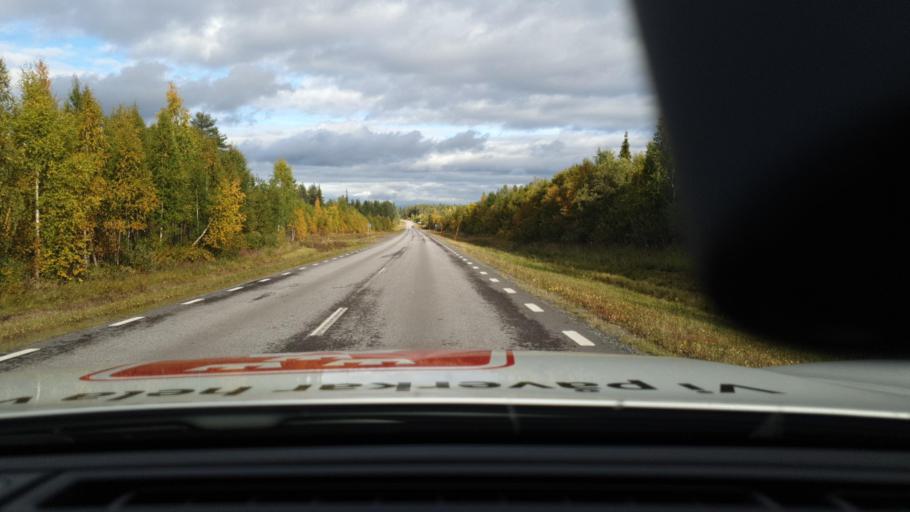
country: SE
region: Norrbotten
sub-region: Gallivare Kommun
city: Gaellivare
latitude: 67.0672
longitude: 21.3024
